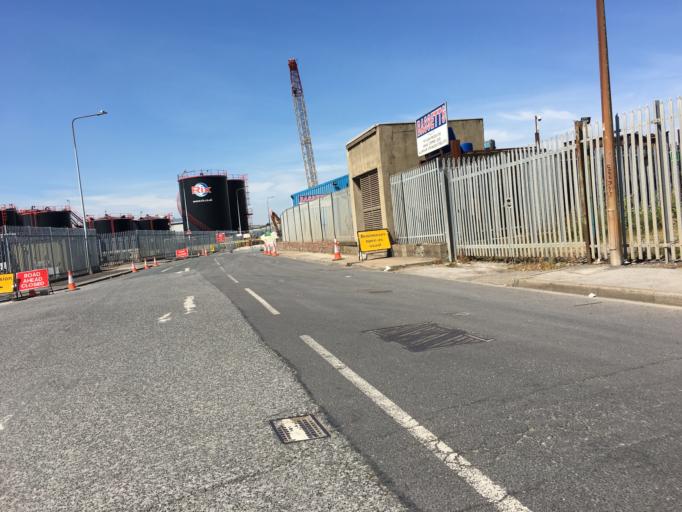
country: GB
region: England
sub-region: City of Kingston upon Hull
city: Hull
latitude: 53.7570
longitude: -0.3345
